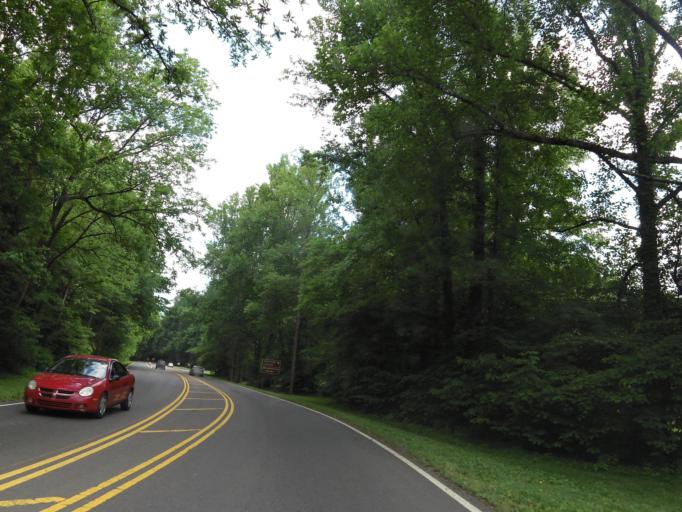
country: US
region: Tennessee
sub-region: Sevier County
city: Gatlinburg
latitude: 35.6862
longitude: -83.5362
